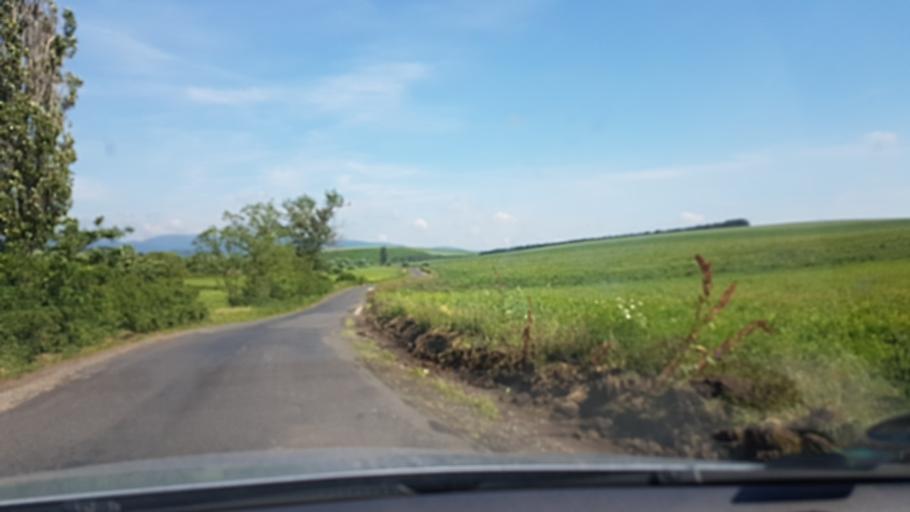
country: HU
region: Borsod-Abauj-Zemplen
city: Saly
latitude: 47.9315
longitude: 20.7115
